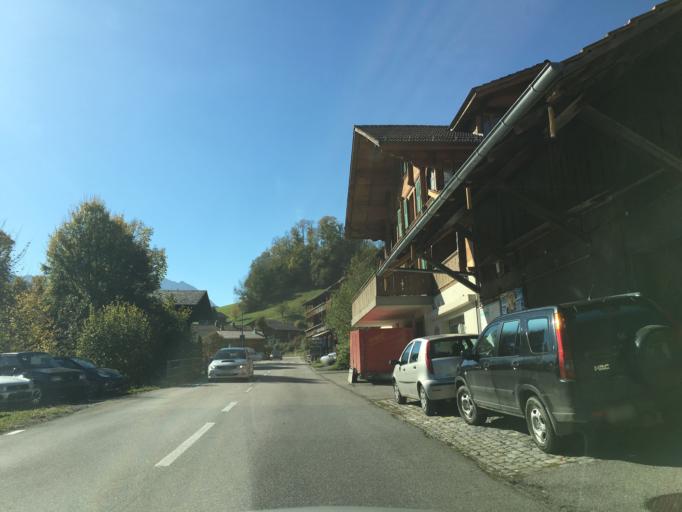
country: CH
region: Bern
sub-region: Frutigen-Niedersimmental District
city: Diemtigen
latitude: 46.6640
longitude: 7.5782
